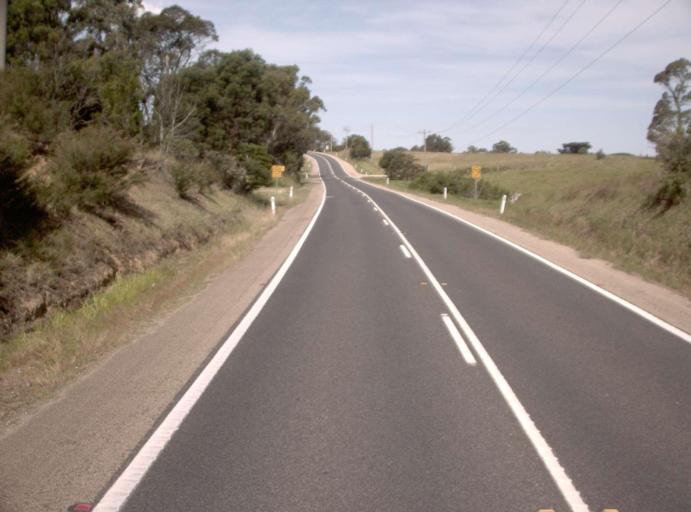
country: AU
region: Victoria
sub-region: East Gippsland
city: Lakes Entrance
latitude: -37.8224
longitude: 147.8494
